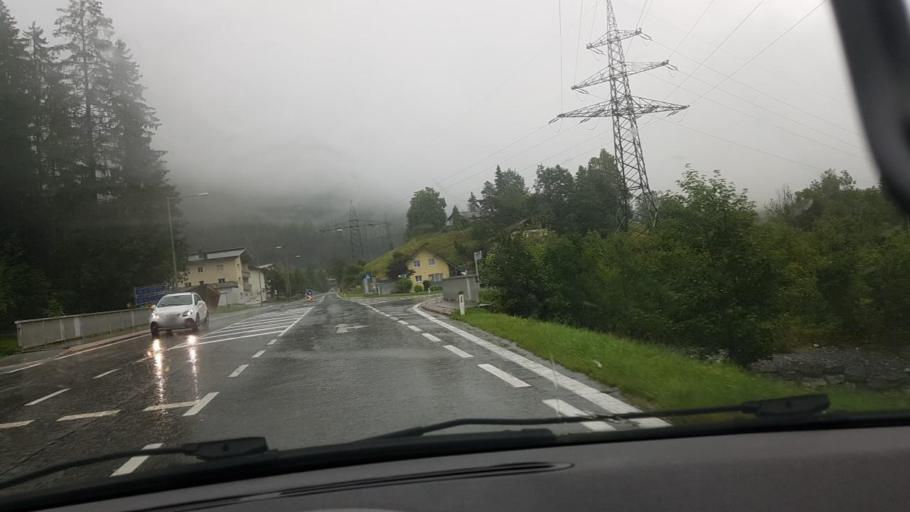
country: AT
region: Vorarlberg
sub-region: Politischer Bezirk Bludenz
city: Klosterle
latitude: 47.1300
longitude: 10.0482
